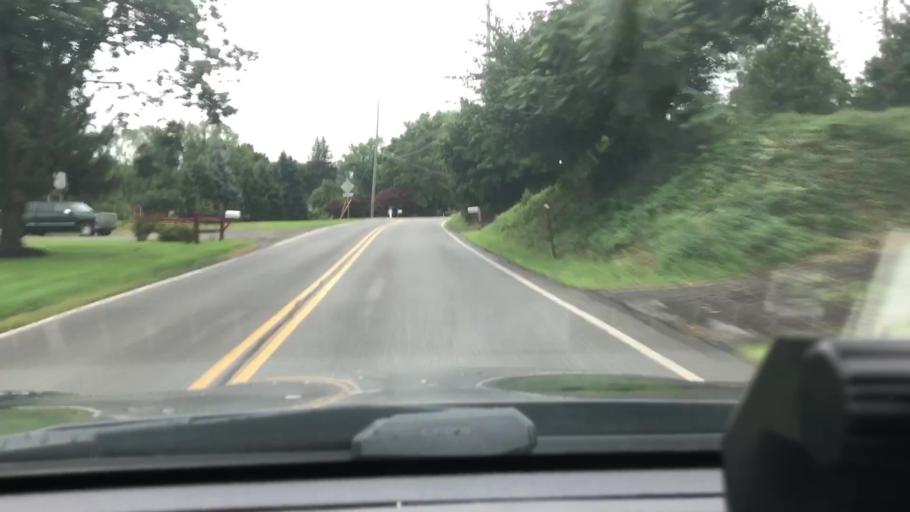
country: US
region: Pennsylvania
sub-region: Montgomery County
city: Gilbertsville
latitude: 40.3019
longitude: -75.6189
